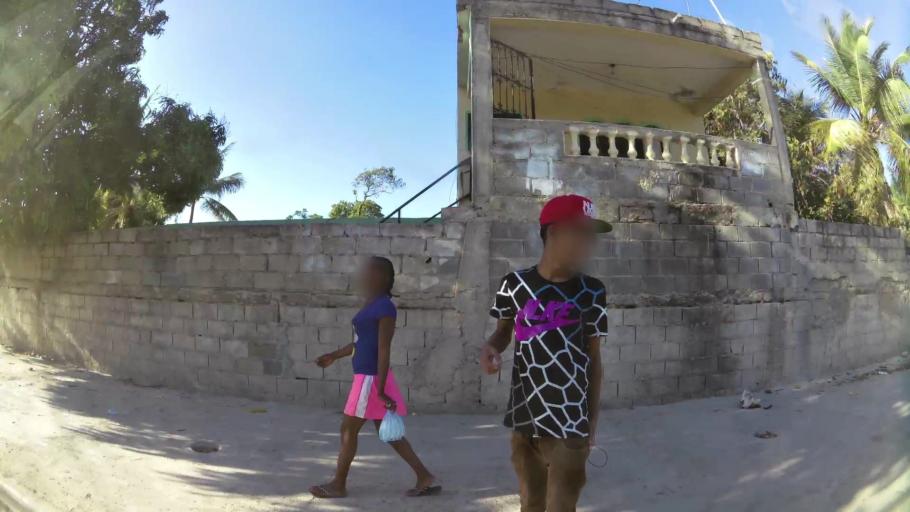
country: DO
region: Santo Domingo
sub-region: Santo Domingo
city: Santo Domingo Este
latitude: 18.4788
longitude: -69.8224
